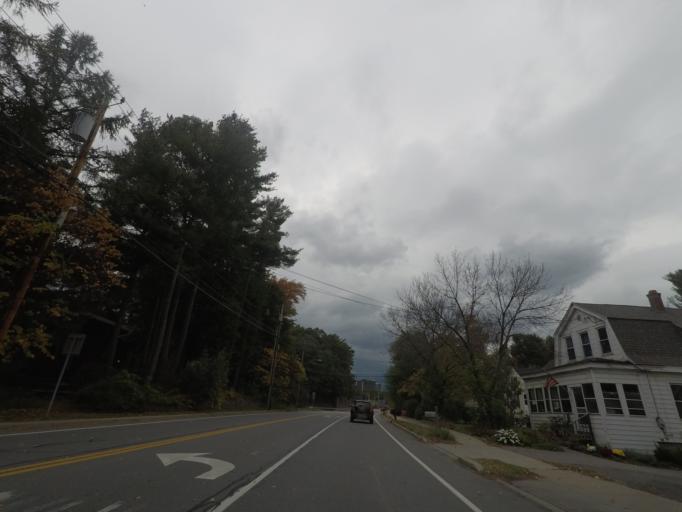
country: US
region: New York
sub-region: Albany County
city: McKownville
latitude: 42.6804
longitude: -73.8437
